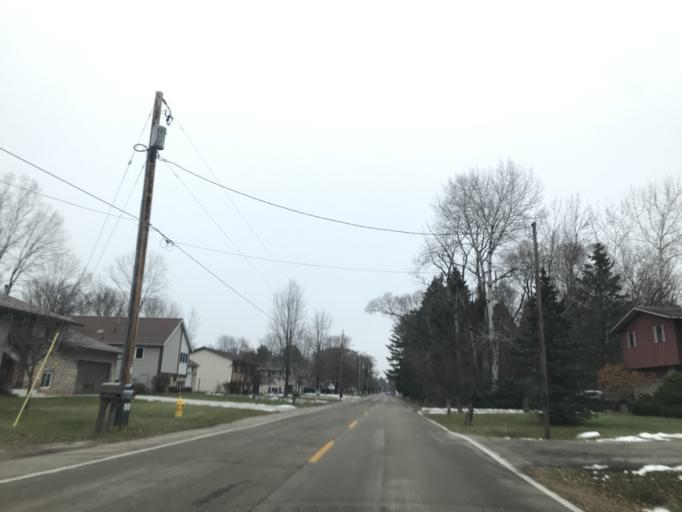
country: US
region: Wisconsin
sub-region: Marinette County
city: Marinette
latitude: 45.0780
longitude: -87.6265
